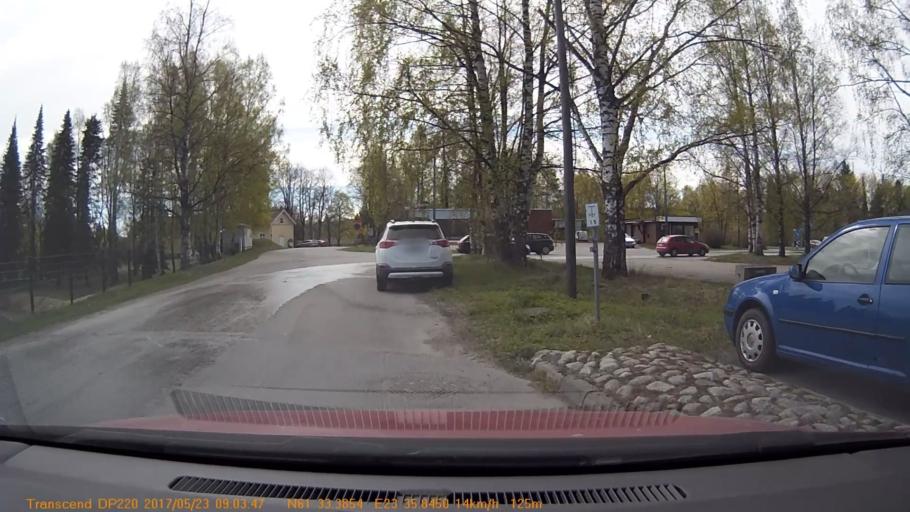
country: FI
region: Pirkanmaa
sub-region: Tampere
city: Yloejaervi
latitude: 61.5564
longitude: 23.5975
